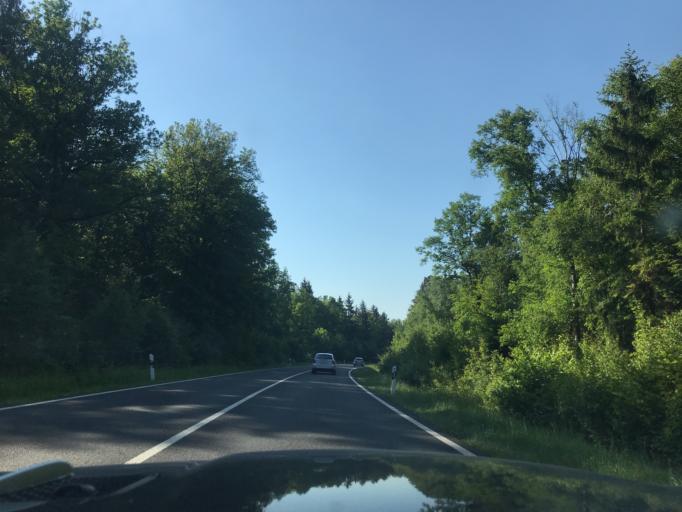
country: DE
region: Thuringia
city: Luisenthal
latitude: 50.7925
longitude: 10.7525
